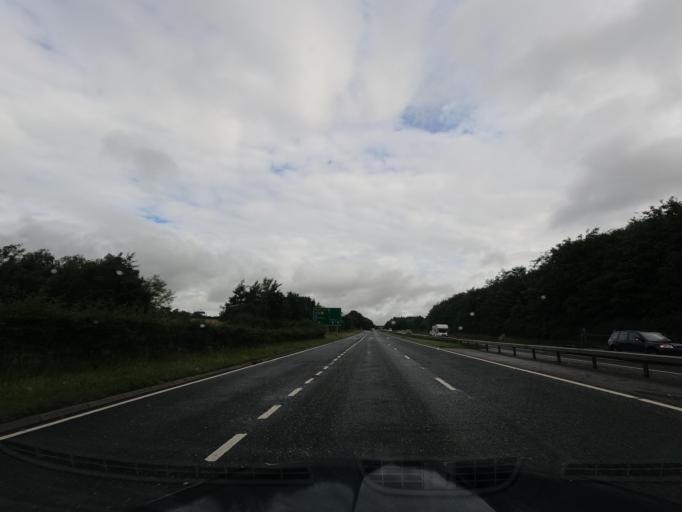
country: GB
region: England
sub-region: Northumberland
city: Morpeth
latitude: 55.1863
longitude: -1.7150
